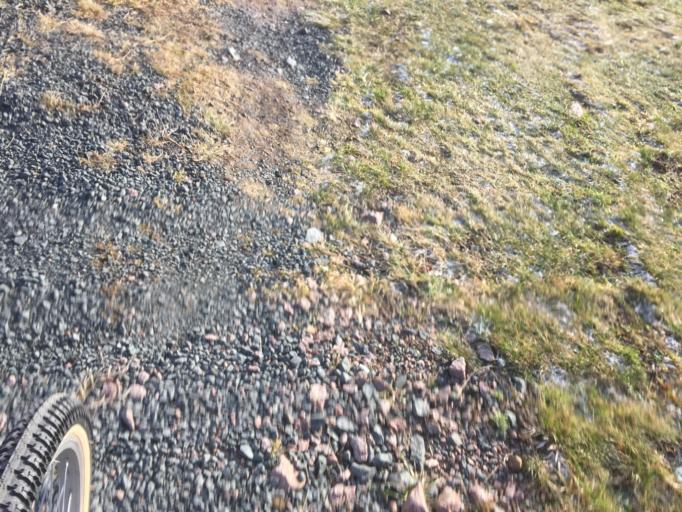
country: SE
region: Joenkoeping
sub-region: Aneby Kommun
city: Aneby
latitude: 57.8285
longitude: 14.8117
